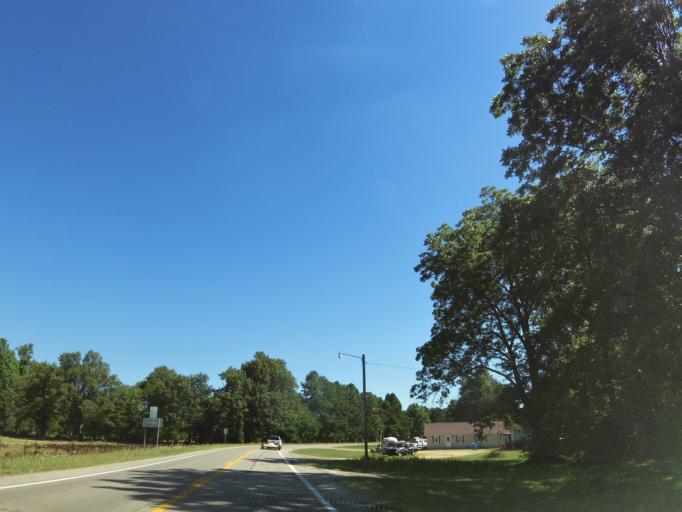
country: US
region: Arkansas
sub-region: Clay County
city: Piggott
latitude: 36.4523
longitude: -90.1471
